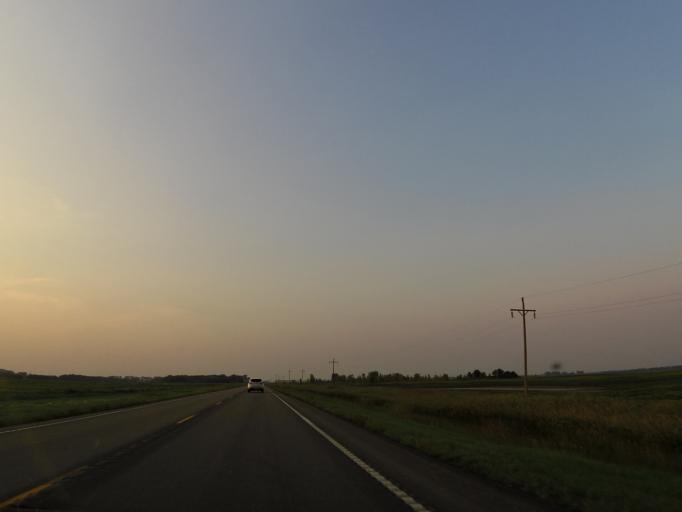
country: US
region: North Dakota
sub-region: Grand Forks County
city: Larimore
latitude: 48.1251
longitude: -97.6225
